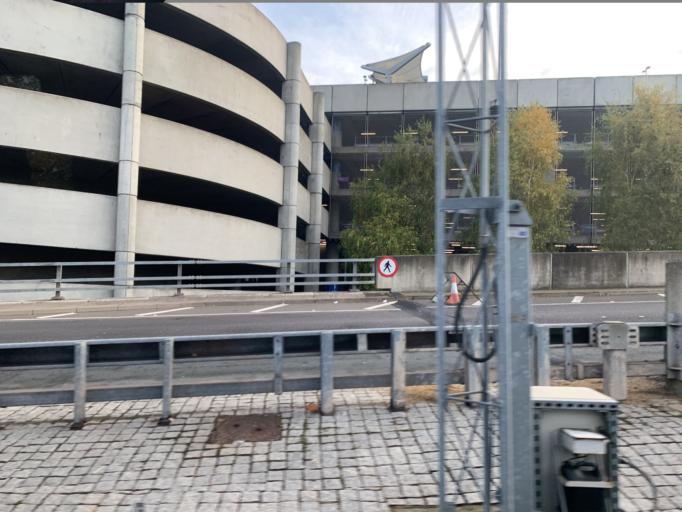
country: GB
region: England
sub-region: Buckinghamshire
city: Iver
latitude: 51.4708
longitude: -0.4908
